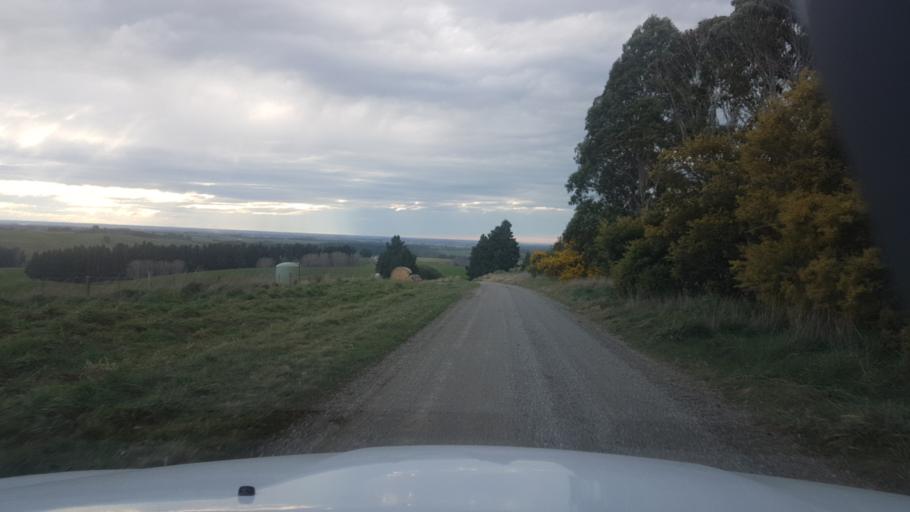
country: NZ
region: Canterbury
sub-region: Timaru District
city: Pleasant Point
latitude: -44.3448
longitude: 171.1367
